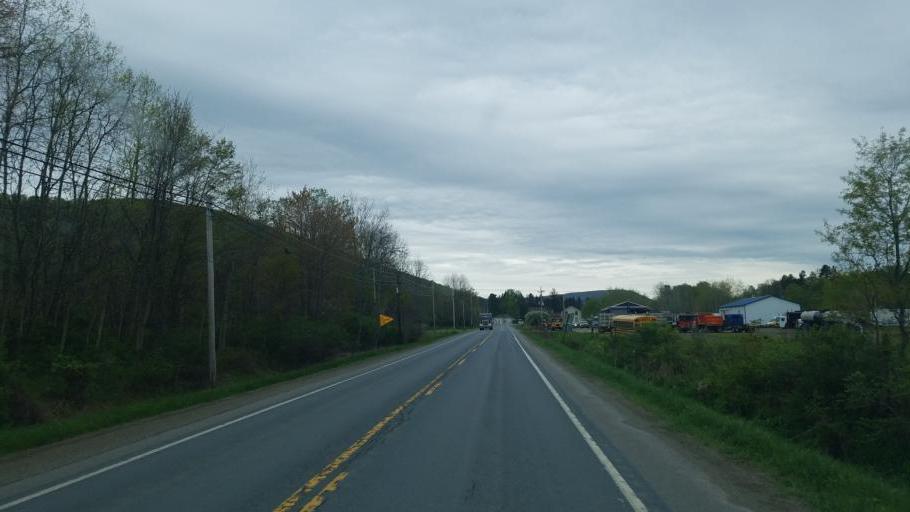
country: US
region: Pennsylvania
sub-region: Tioga County
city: Westfield
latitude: 41.9361
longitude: -77.4876
